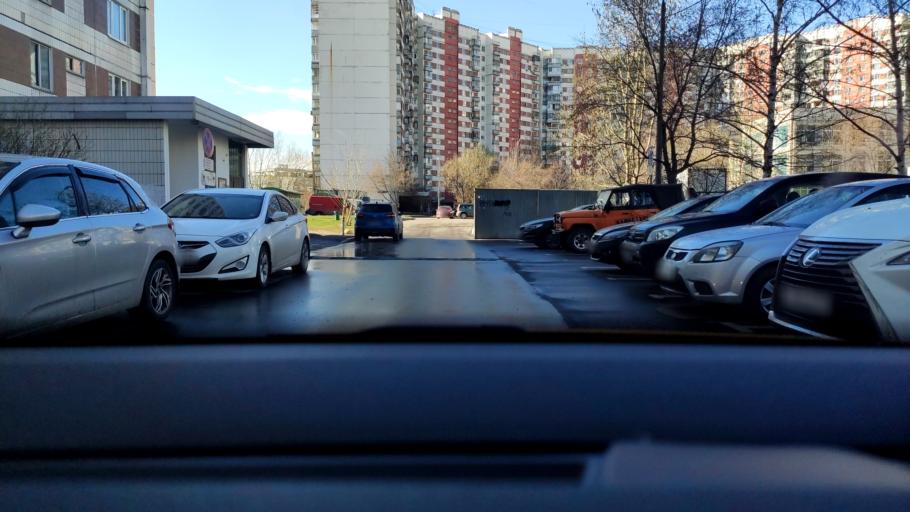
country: RU
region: Moskovskaya
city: Reutov
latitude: 55.7407
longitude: 37.8509
